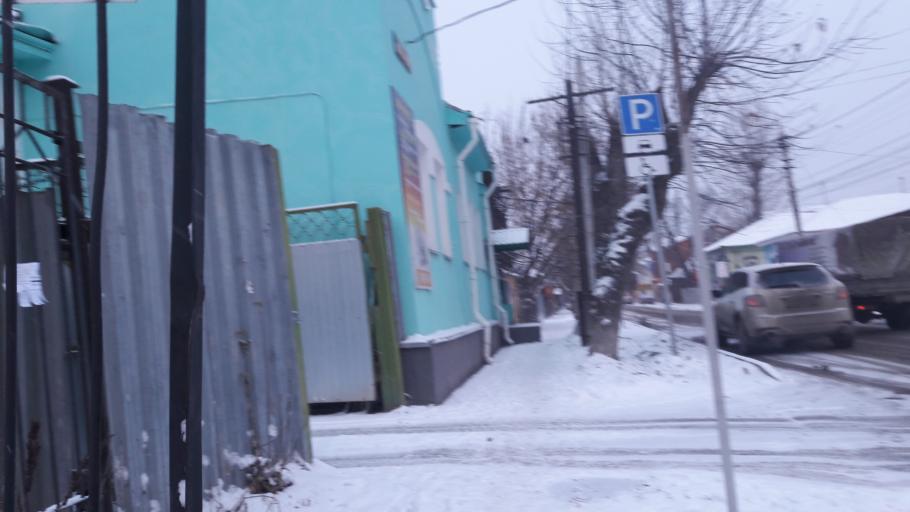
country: RU
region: Tula
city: Tula
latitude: 54.1879
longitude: 37.6175
